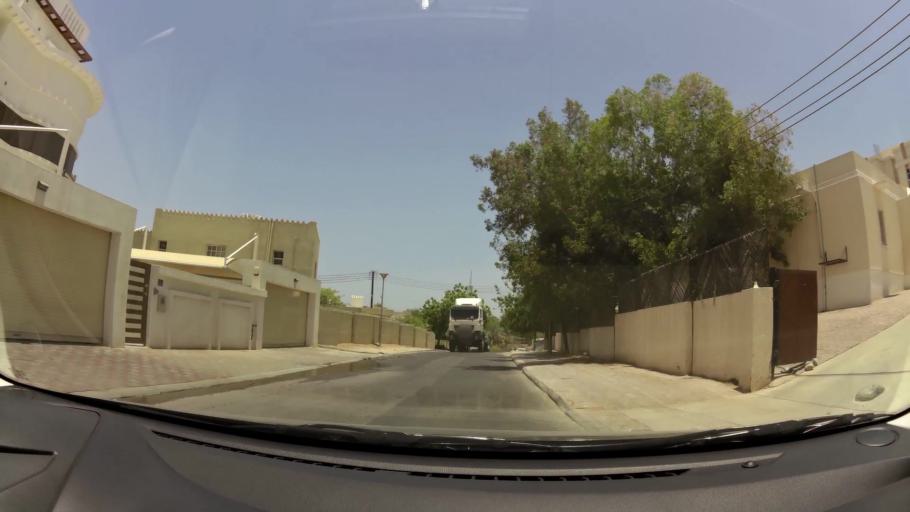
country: OM
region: Muhafazat Masqat
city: Bawshar
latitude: 23.6031
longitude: 58.4531
